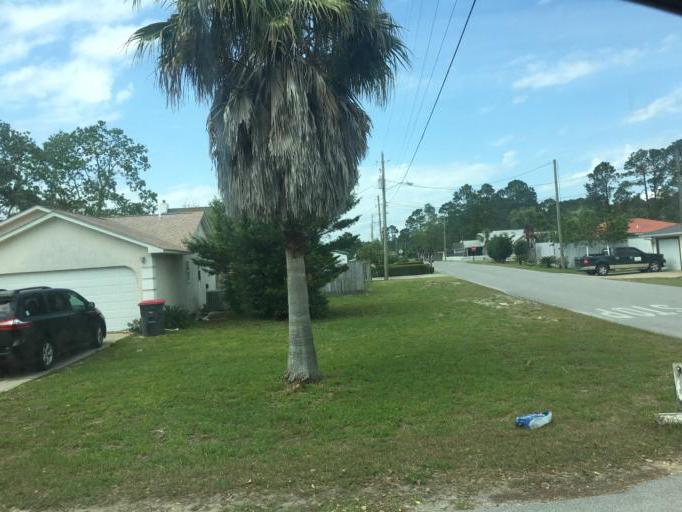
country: US
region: Florida
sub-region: Bay County
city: Laguna Beach
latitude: 30.2314
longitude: -85.8886
